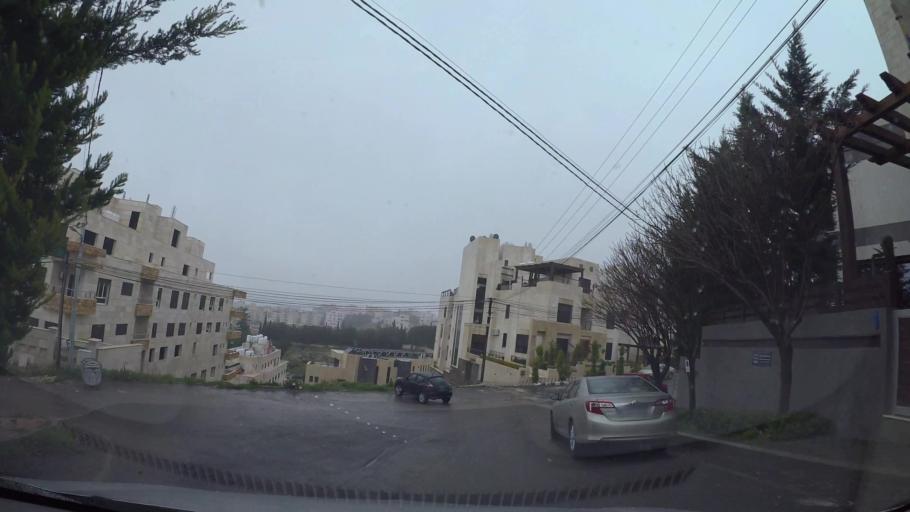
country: JO
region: Amman
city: Al Jubayhah
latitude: 32.0079
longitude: 35.8292
